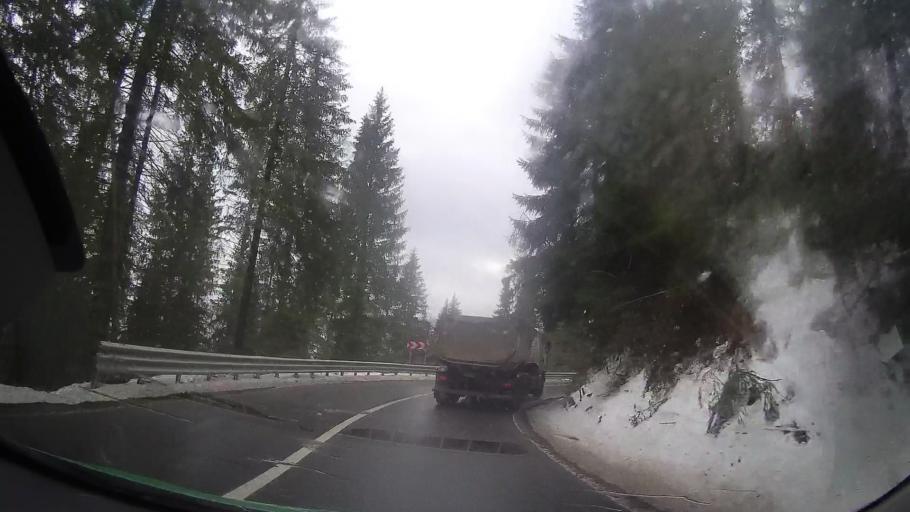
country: RO
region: Harghita
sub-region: Municipiul Gheorgheni
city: Gheorgheni
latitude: 46.7788
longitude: 25.7272
